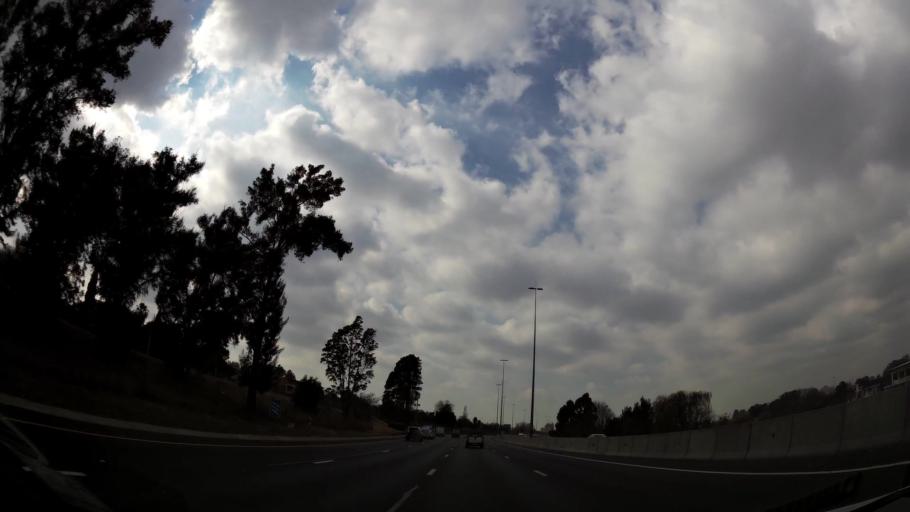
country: ZA
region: Gauteng
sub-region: Ekurhuleni Metropolitan Municipality
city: Benoni
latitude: -26.1807
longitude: 28.3035
